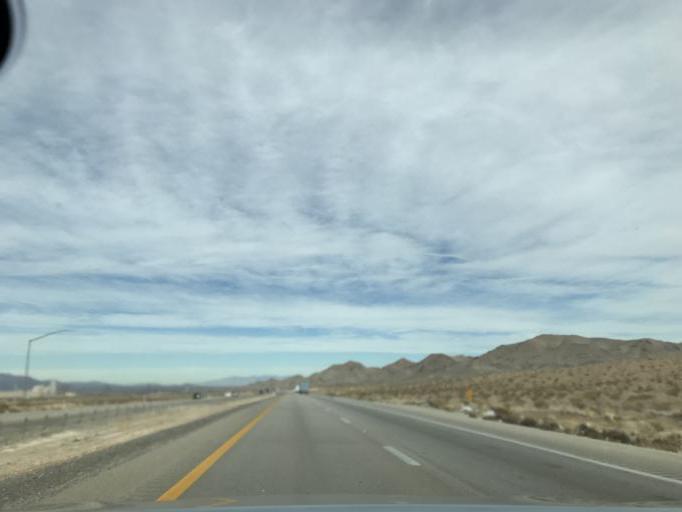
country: US
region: Nevada
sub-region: Clark County
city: Nellis Air Force Base
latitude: 36.3379
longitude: -114.9172
